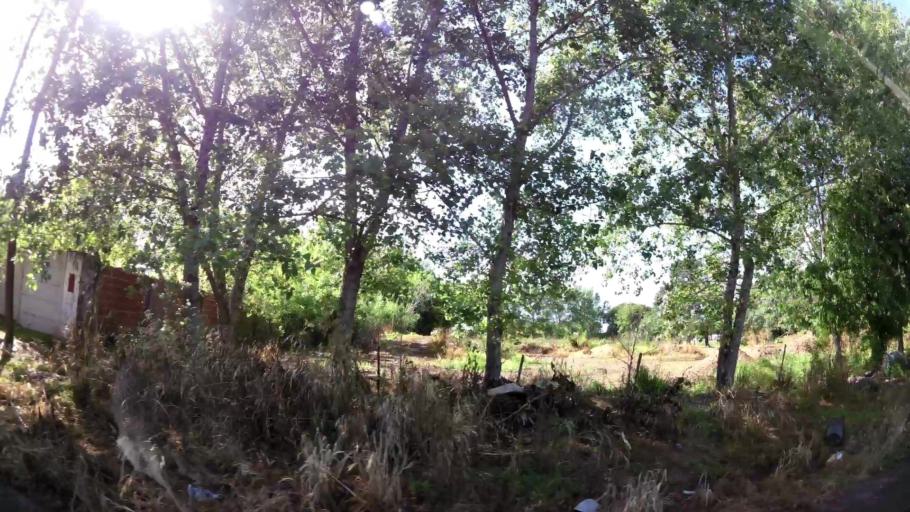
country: AR
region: Buenos Aires
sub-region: Partido de Quilmes
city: Quilmes
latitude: -34.7980
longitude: -58.1382
